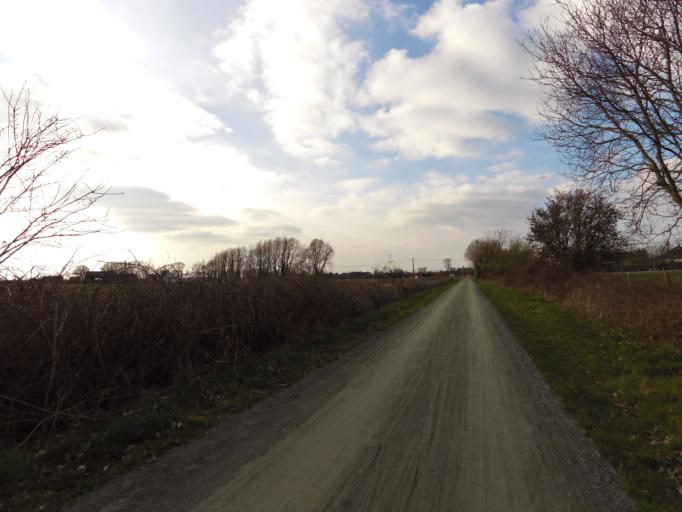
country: BE
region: Flanders
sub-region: Provincie West-Vlaanderen
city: Ichtegem
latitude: 51.1198
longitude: 3.0285
